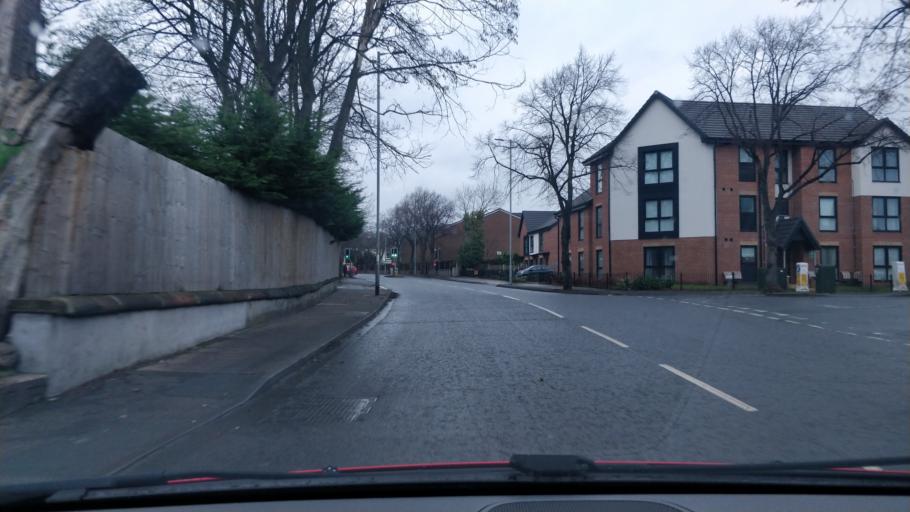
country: GB
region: England
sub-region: Sefton
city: Litherland
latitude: 53.4725
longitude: -2.9984
